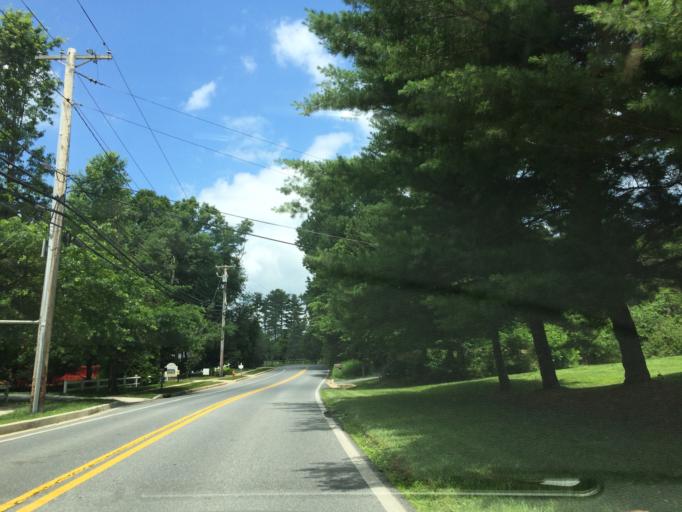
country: US
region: Maryland
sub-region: Howard County
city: Ellicott City
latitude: 39.2868
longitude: -76.8296
